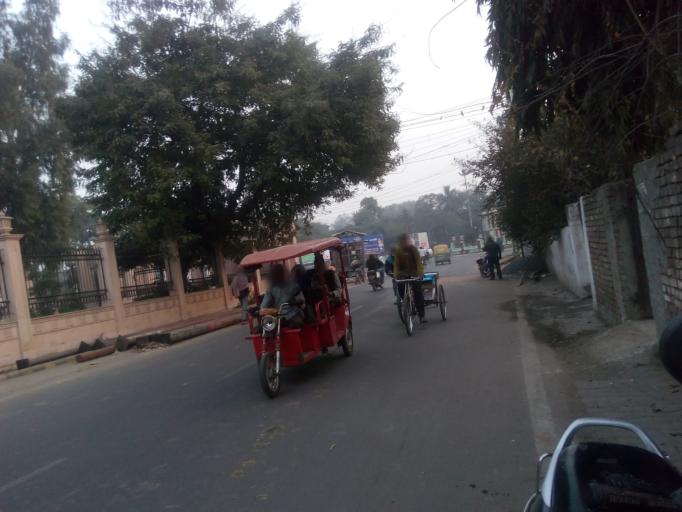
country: IN
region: Uttar Pradesh
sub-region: Aligarh
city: Aligarh
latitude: 27.8948
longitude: 78.0737
